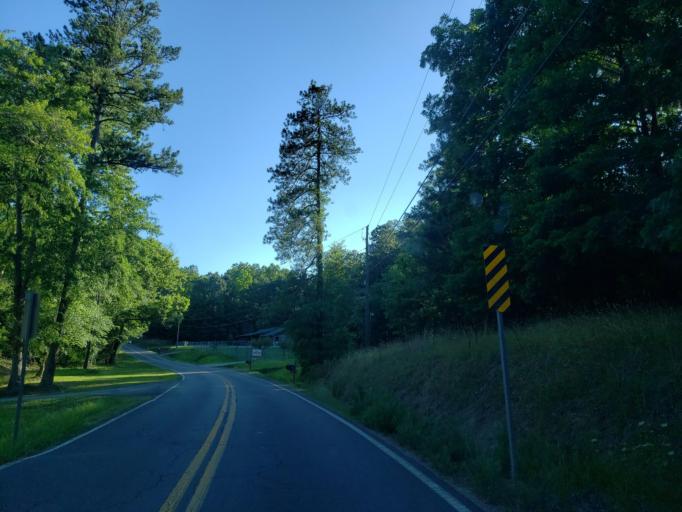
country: US
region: Georgia
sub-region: Floyd County
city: Shannon
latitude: 34.3856
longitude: -85.1255
